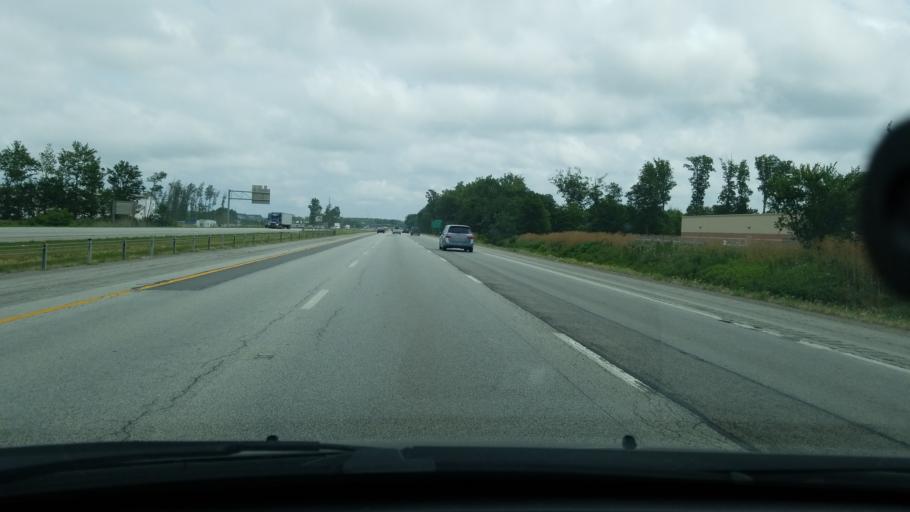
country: US
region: Ohio
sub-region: Lorain County
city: Avon Center
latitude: 41.4643
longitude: -82.0112
